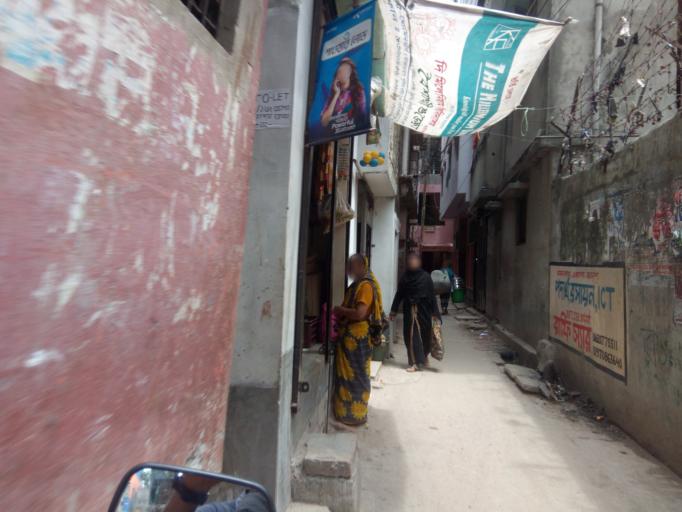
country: BD
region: Dhaka
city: Azimpur
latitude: 23.7299
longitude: 90.3728
